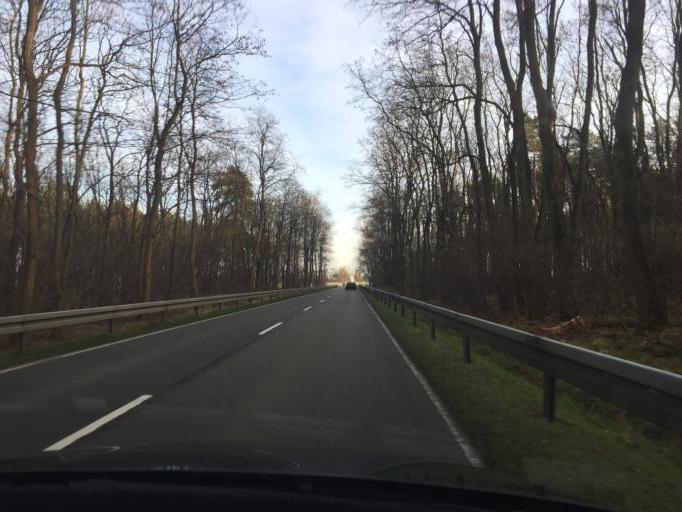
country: DE
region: Brandenburg
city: Heinersbruck
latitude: 51.7272
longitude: 14.5236
